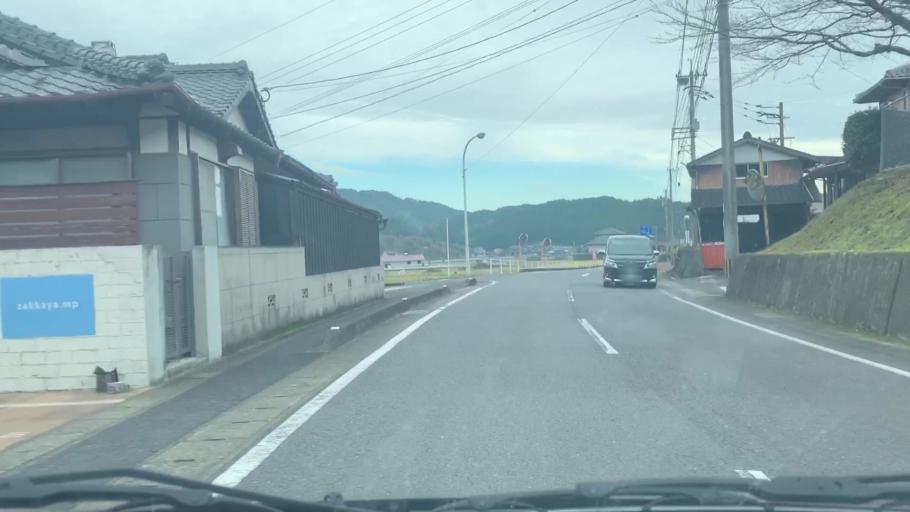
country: JP
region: Saga Prefecture
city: Ureshinomachi-shimojuku
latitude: 33.1344
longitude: 129.9741
